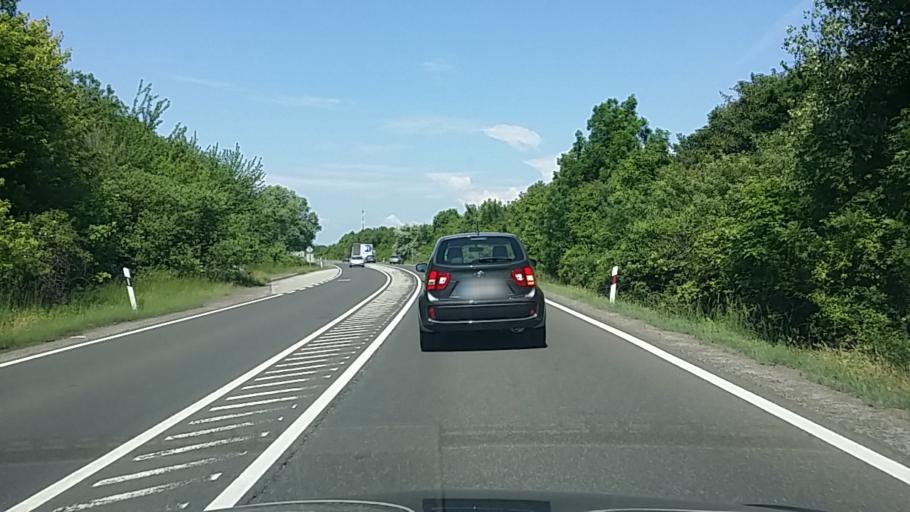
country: HU
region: Nograd
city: Nagyoroszi
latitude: 48.0464
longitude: 19.0454
